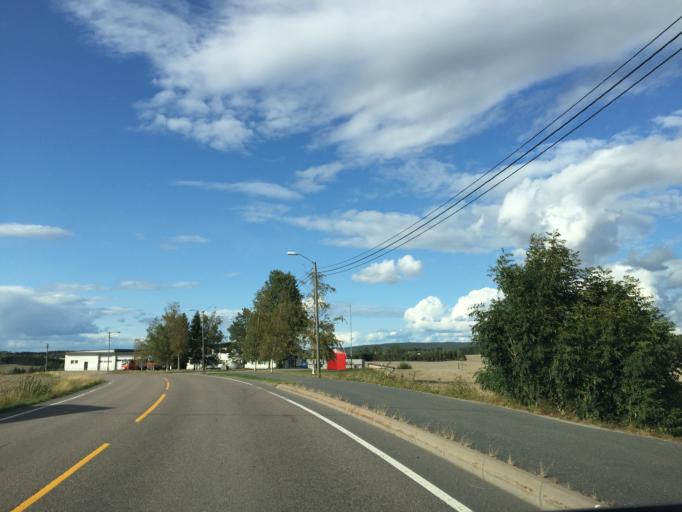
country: NO
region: Ostfold
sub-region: Trogstad
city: Skjonhaug
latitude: 59.6438
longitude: 11.3159
